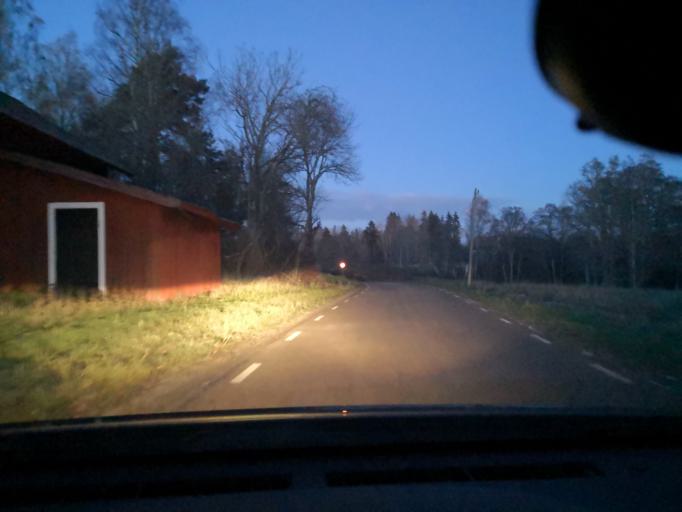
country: SE
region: Vaestmanland
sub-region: Sala Kommun
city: Sala
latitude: 59.8732
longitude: 16.7221
